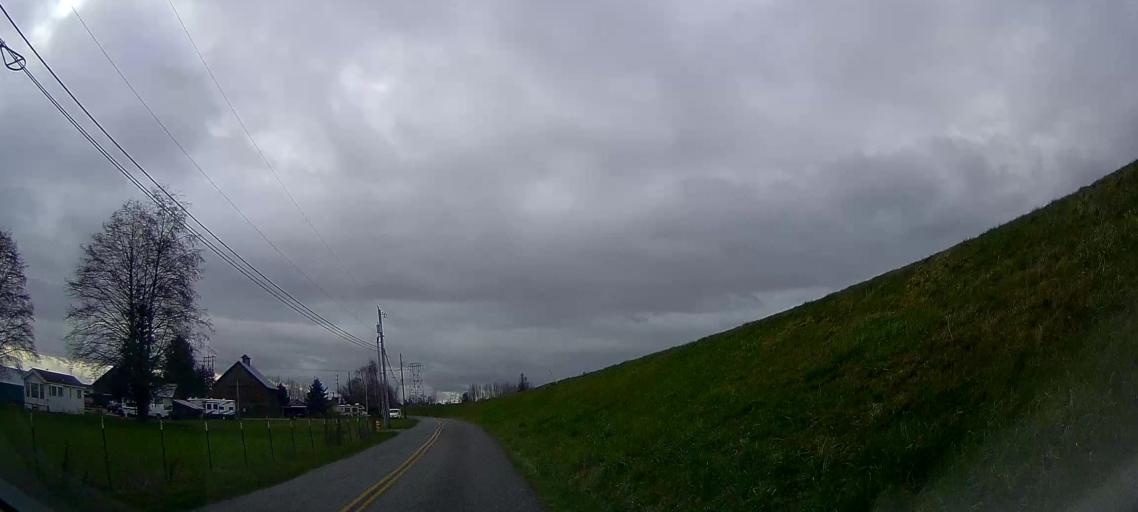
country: US
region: Washington
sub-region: Skagit County
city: Mount Vernon
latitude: 48.4439
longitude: -122.3693
